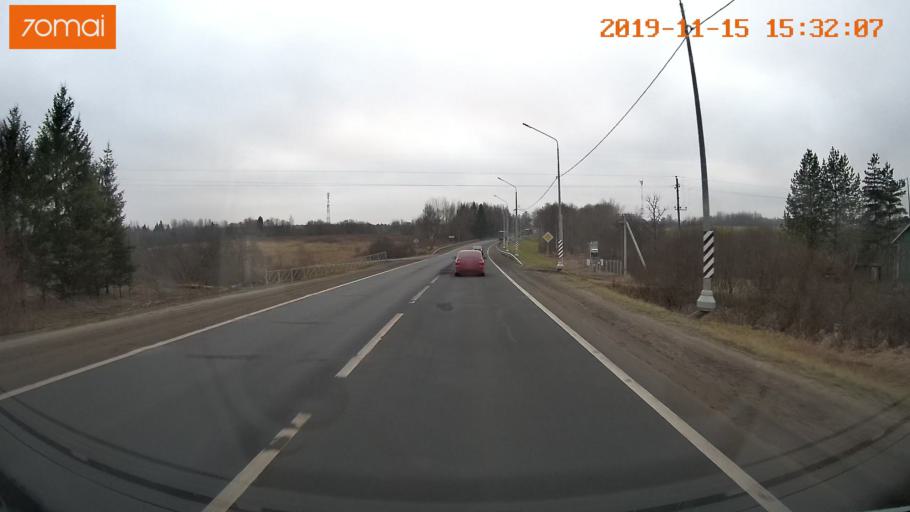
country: RU
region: Jaroslavl
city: Danilov
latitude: 58.0932
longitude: 40.1032
